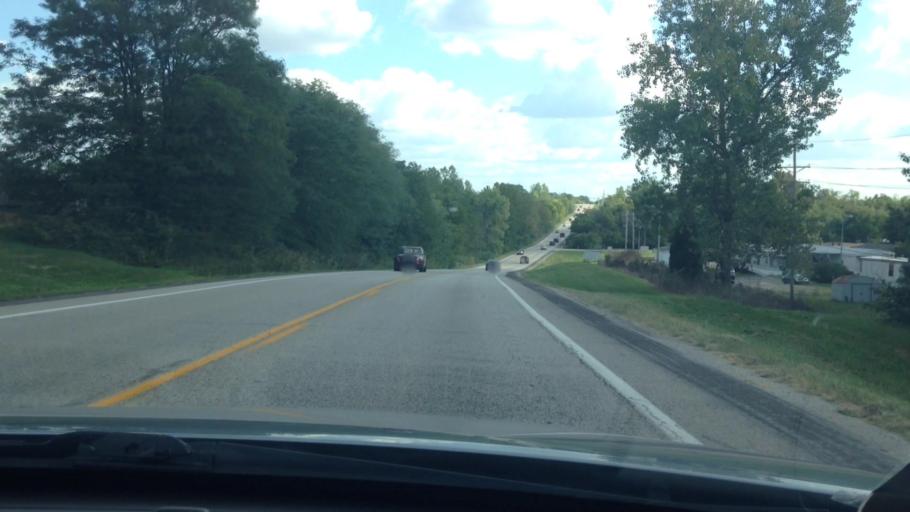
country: US
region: Missouri
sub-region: Clay County
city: Liberty
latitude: 39.2870
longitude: -94.4708
